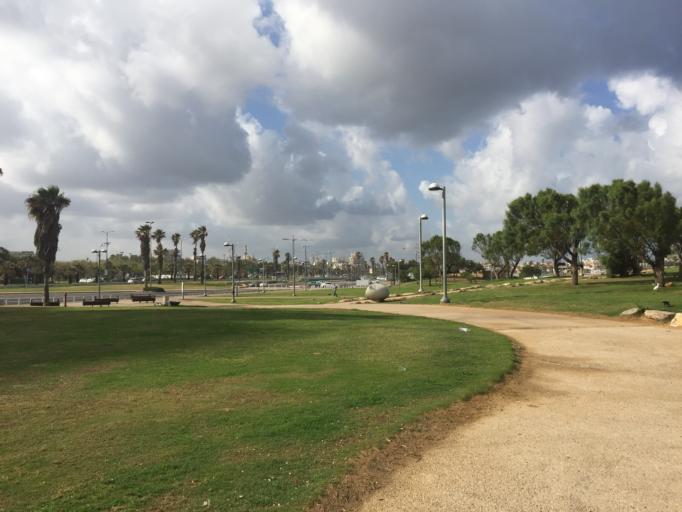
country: IL
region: Tel Aviv
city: Yafo
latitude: 32.0632
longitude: 34.7607
